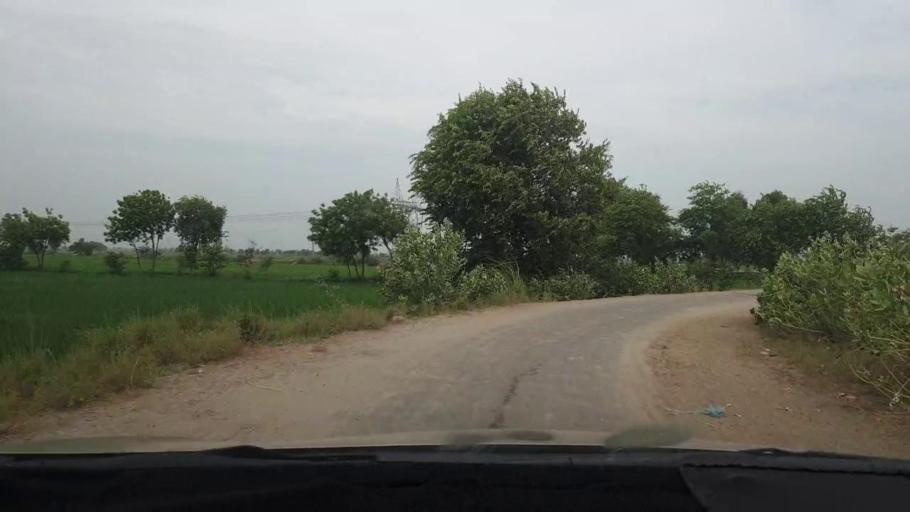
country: PK
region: Sindh
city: Naudero
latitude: 27.6792
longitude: 68.3401
